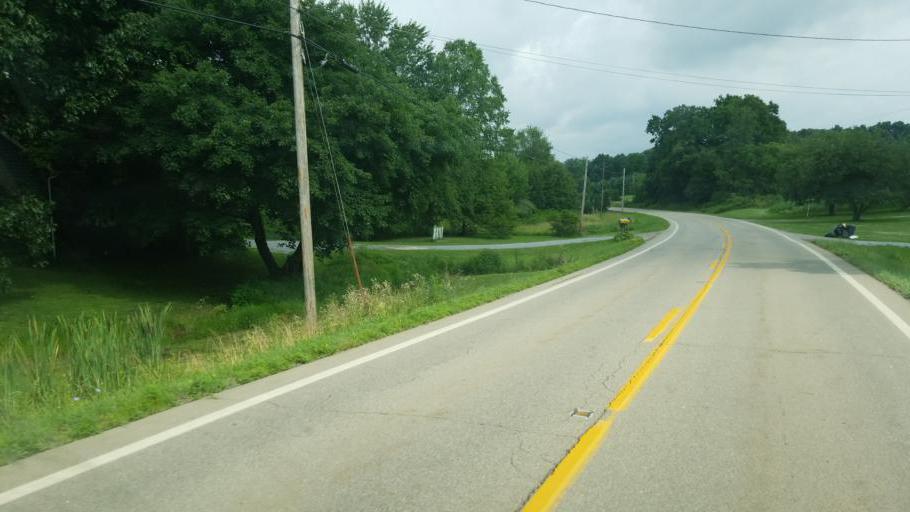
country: US
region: Ohio
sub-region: Columbiana County
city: Salineville
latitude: 40.6862
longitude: -80.8033
